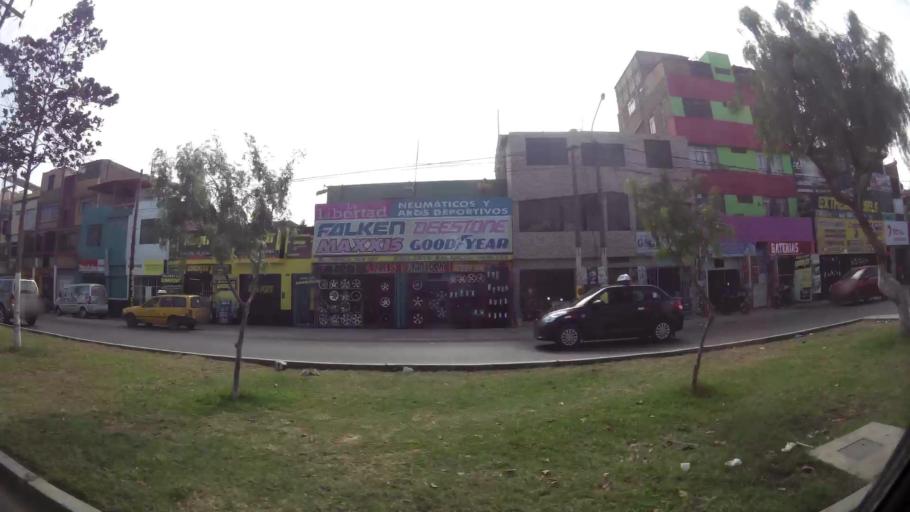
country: PE
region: La Libertad
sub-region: Provincia de Trujillo
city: Trujillo
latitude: -8.1111
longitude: -79.0132
